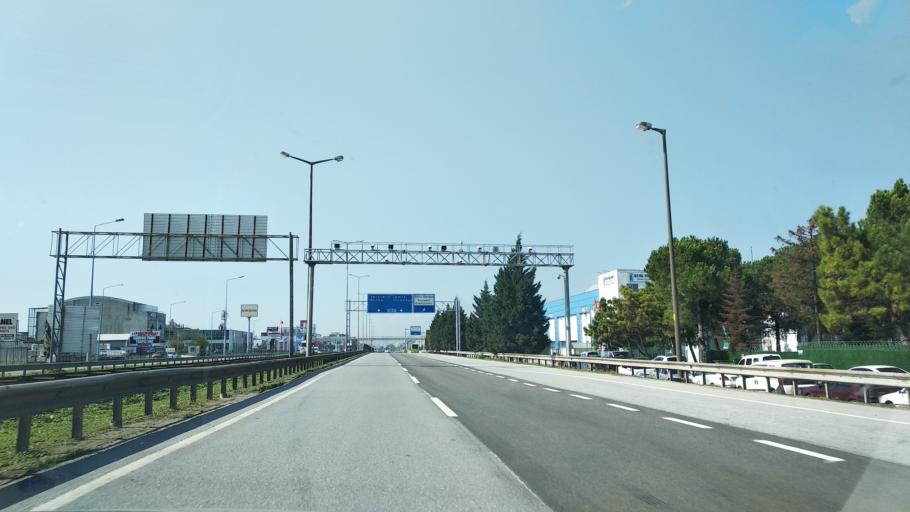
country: TR
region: Kocaeli
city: Kosekoy
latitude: 40.7522
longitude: 30.0323
